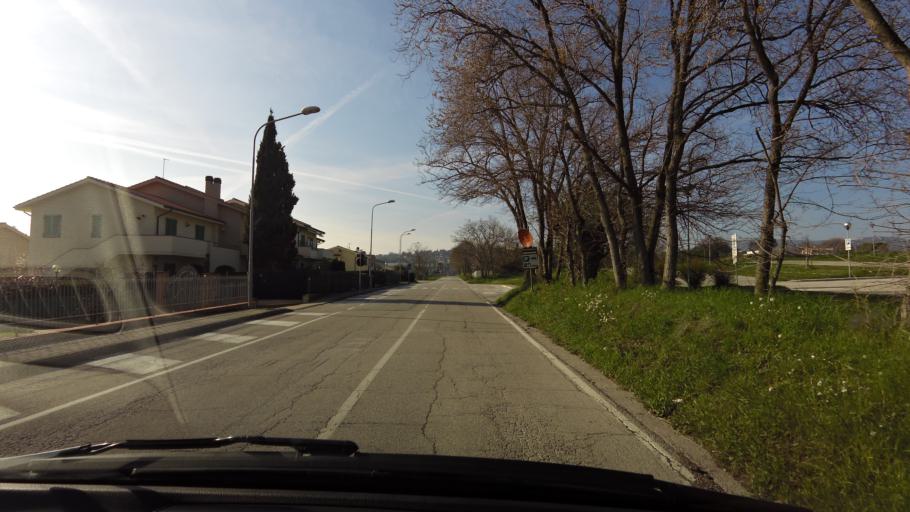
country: IT
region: The Marches
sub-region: Provincia di Ancona
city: Marcelli
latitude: 43.4971
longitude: 13.6212
